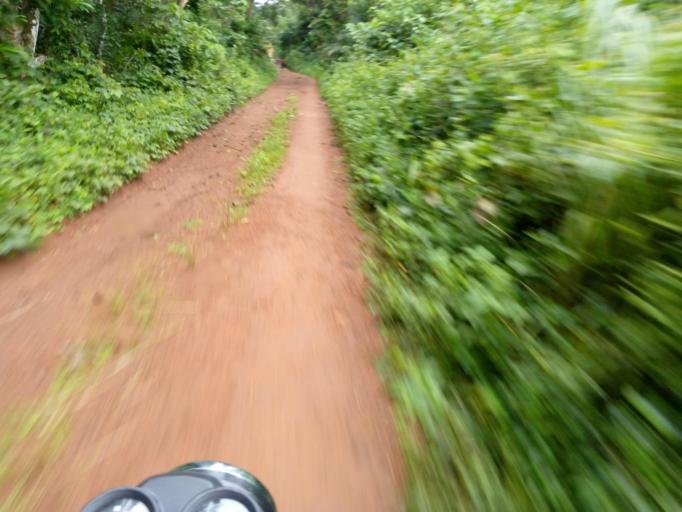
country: SL
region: Eastern Province
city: Buedu
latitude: 8.4700
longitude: -10.3471
